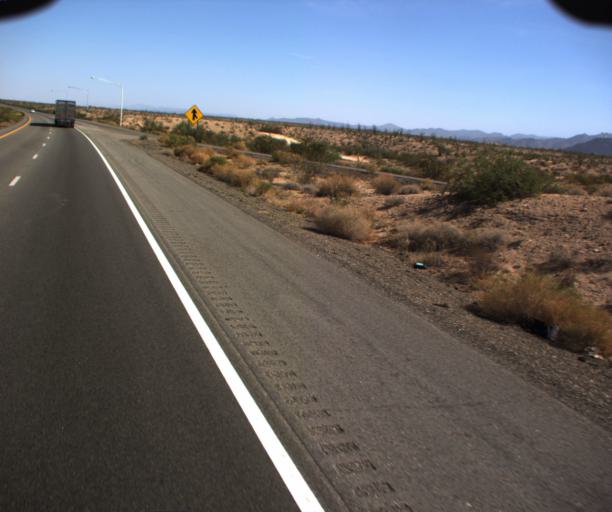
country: US
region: Arizona
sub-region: Mohave County
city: Kingman
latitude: 34.8803
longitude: -114.1480
